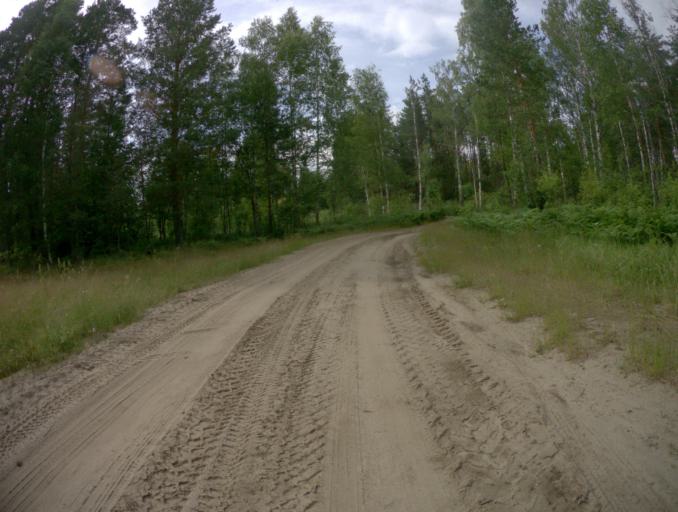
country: RU
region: Vladimir
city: Gorokhovets
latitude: 56.3008
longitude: 42.6607
